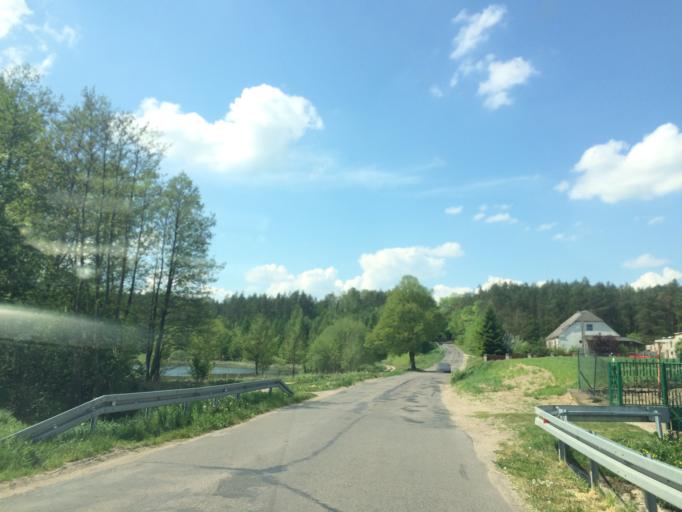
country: PL
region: Warmian-Masurian Voivodeship
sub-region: Powiat nowomiejski
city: Nowe Miasto Lubawskie
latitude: 53.4267
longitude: 19.6868
